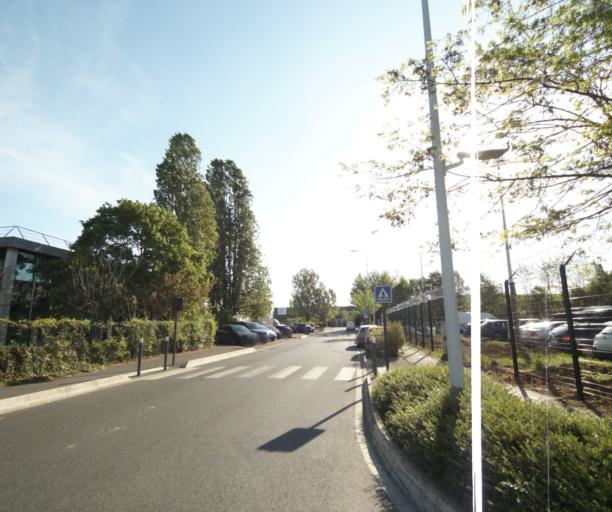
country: FR
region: Ile-de-France
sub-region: Departement de Seine-et-Marne
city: Torcy
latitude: 48.8431
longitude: 2.6585
